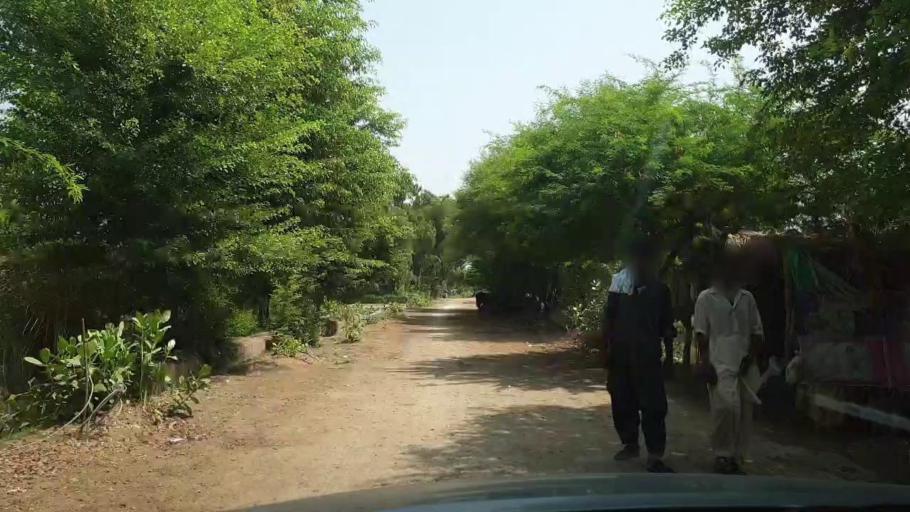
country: PK
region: Sindh
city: Madeji
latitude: 27.7891
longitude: 68.5282
